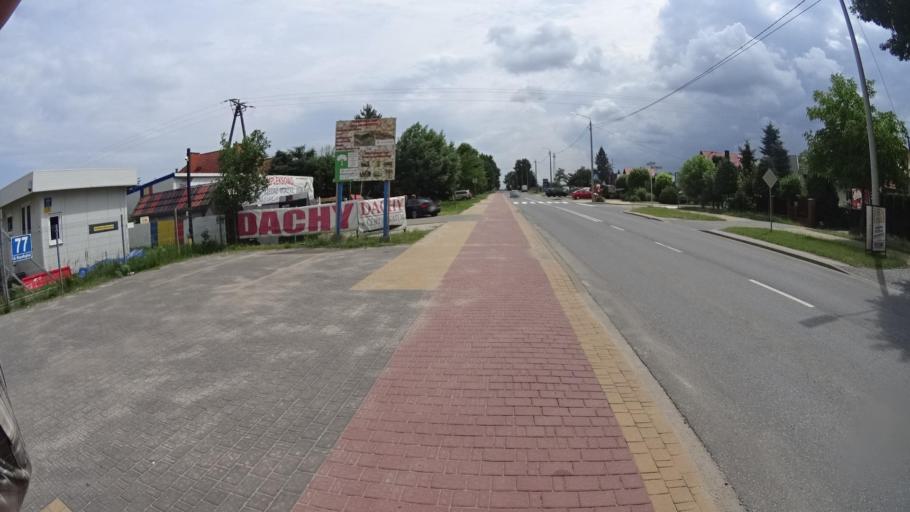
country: PL
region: Masovian Voivodeship
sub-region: Powiat grojecki
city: Grojec
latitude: 51.8531
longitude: 20.8715
